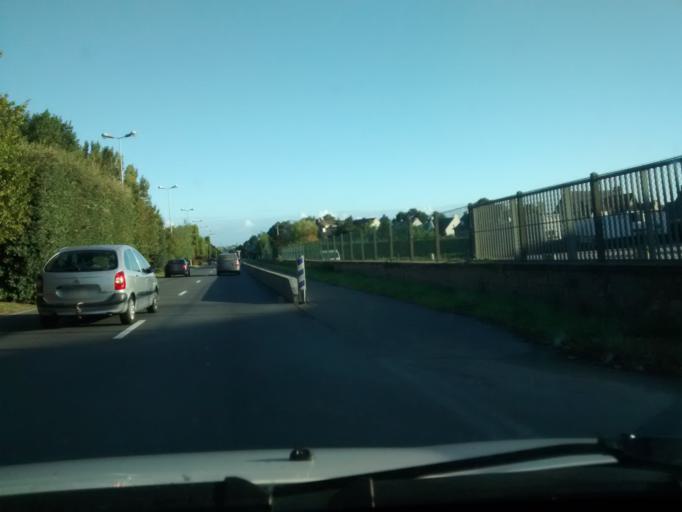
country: FR
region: Brittany
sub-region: Departement d'Ille-et-Vilaine
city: Saint-Jouan-des-Guerets
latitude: 48.6287
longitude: -1.9888
